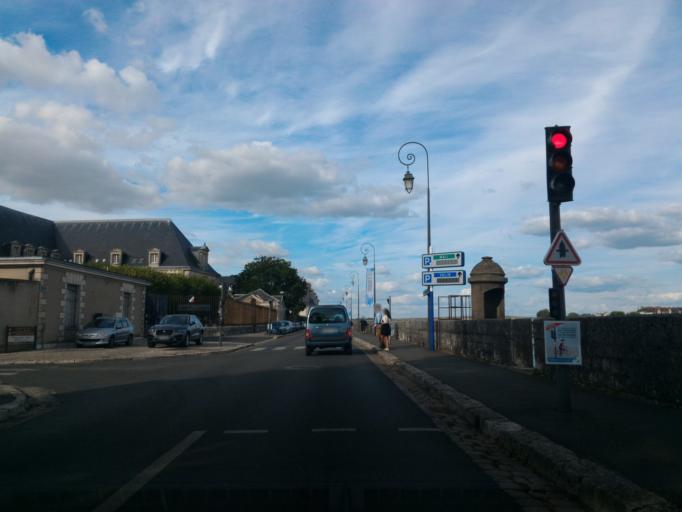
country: FR
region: Centre
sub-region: Departement du Loir-et-Cher
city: Blois
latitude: 47.5826
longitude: 1.3313
